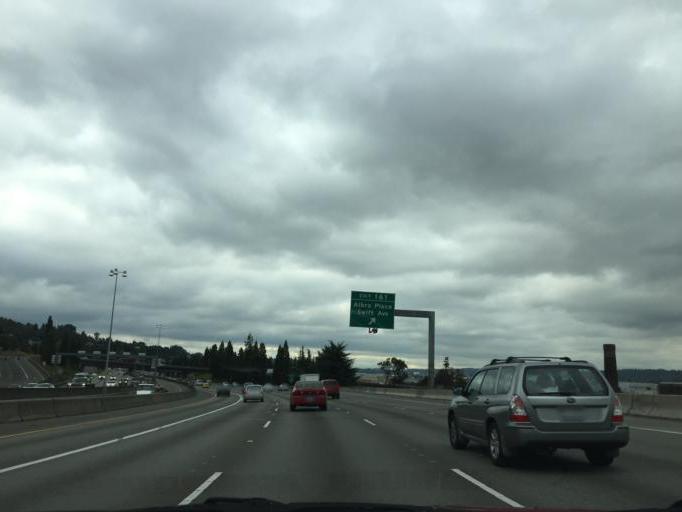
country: US
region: Washington
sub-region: King County
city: White Center
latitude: 47.5518
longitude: -122.3172
